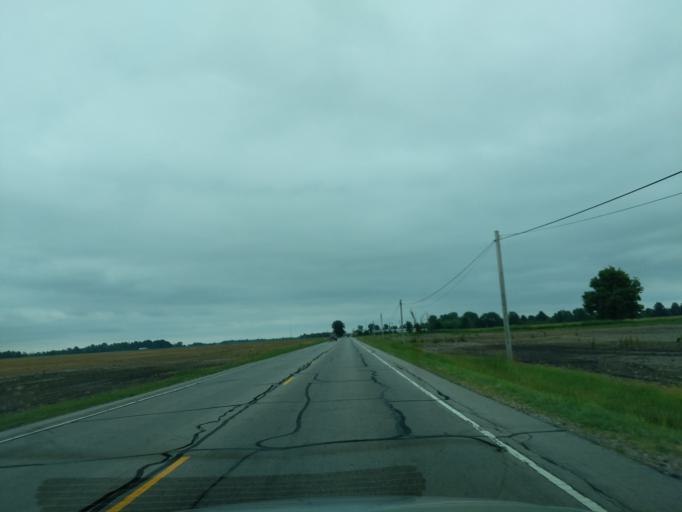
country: US
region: Indiana
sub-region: Madison County
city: Alexandria
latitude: 40.2773
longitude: -85.5749
